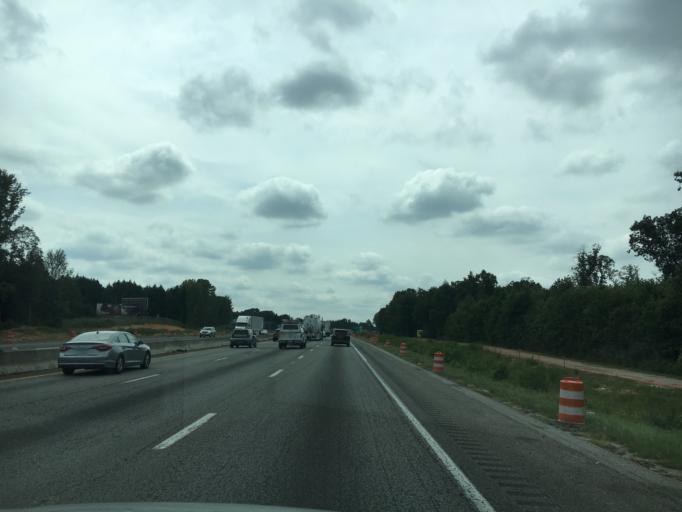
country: US
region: South Carolina
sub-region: Greenville County
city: Five Forks
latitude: 34.8478
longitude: -82.2800
